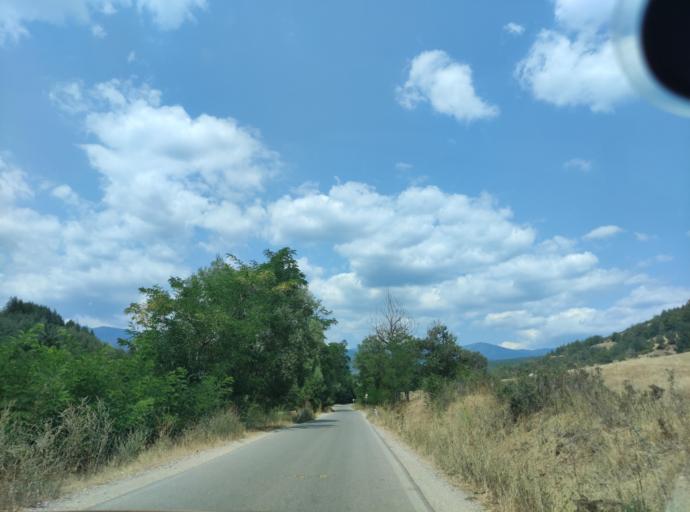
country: BG
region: Blagoevgrad
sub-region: Obshtina Belitsa
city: Belitsa
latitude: 41.9722
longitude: 23.5555
